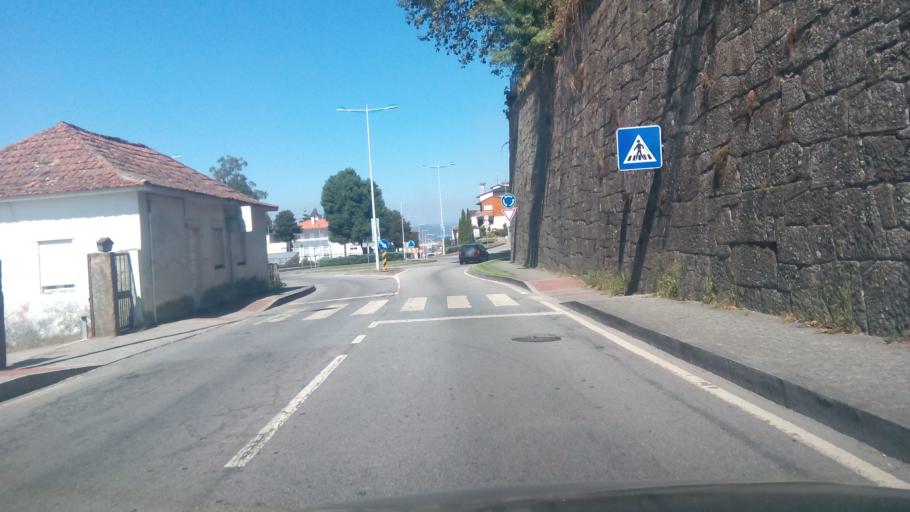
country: PT
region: Porto
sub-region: Penafiel
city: Penafiel
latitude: 41.2019
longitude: -8.2903
